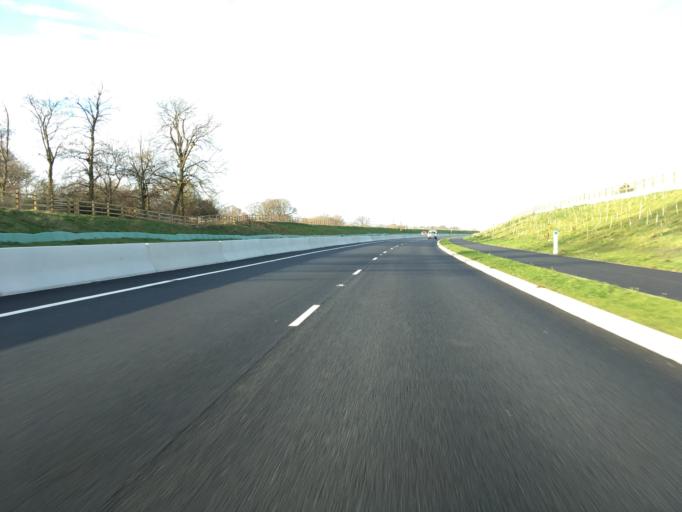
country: GB
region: England
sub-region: Cheshire East
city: Wilmslow
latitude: 53.3571
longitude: -2.2333
